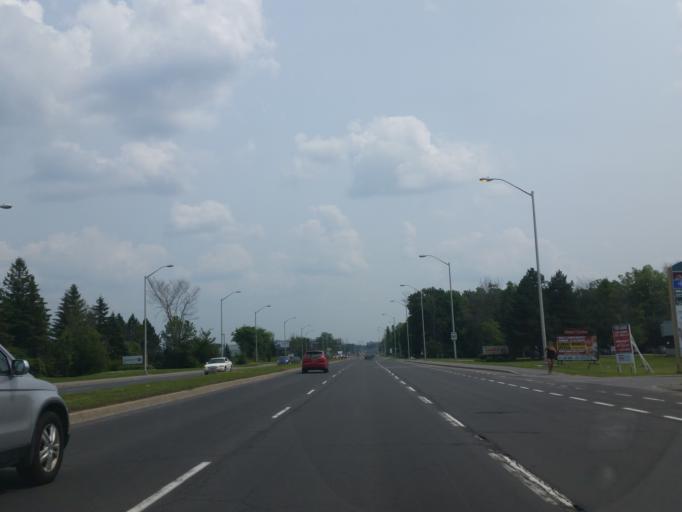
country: CA
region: Ontario
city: Bells Corners
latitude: 45.3478
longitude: -75.9235
